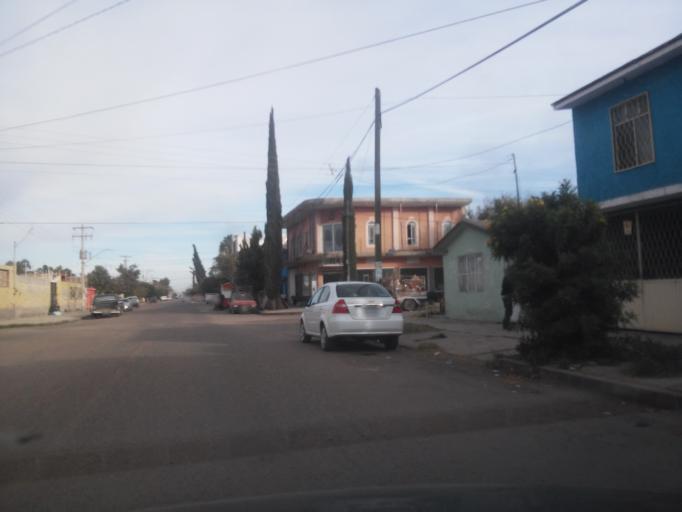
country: MX
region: Durango
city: Victoria de Durango
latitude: 24.0246
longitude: -104.6383
